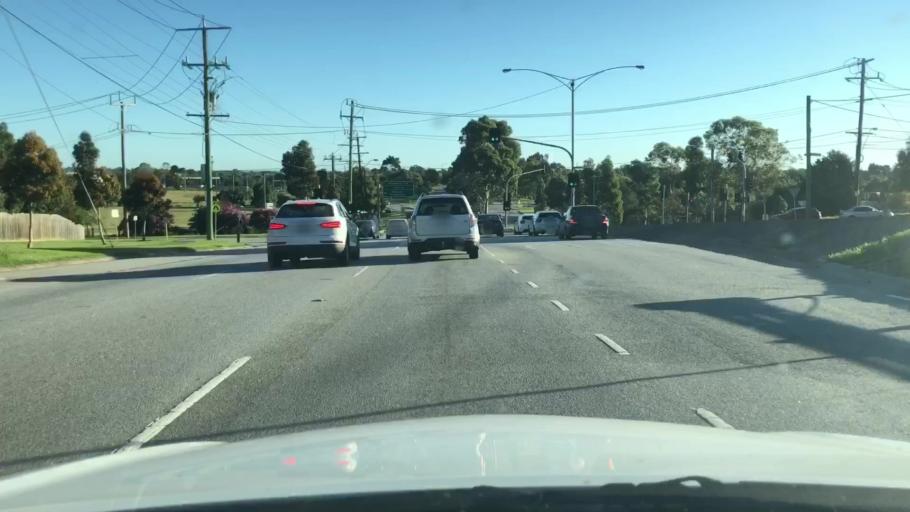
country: AU
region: Victoria
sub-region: Greater Dandenong
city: Dandenong North
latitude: -37.9548
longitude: 145.2265
